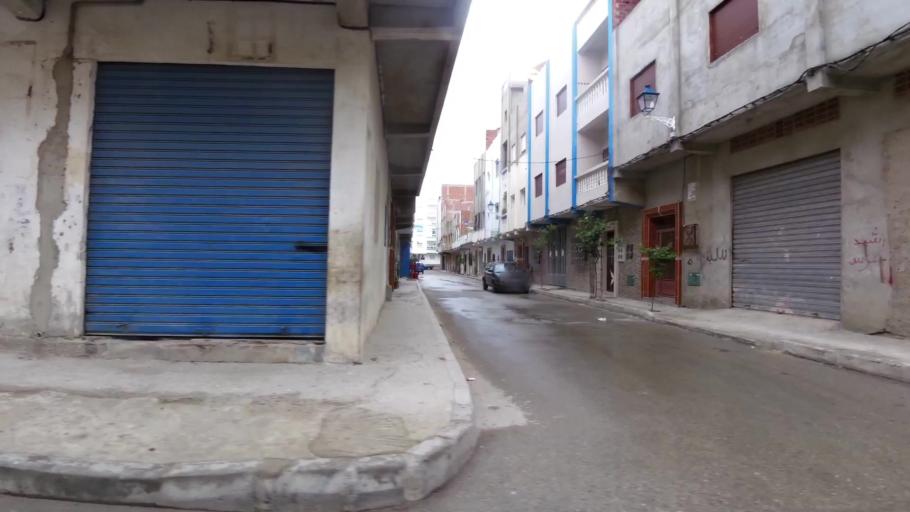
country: MA
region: Tanger-Tetouan
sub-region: Tetouan
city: Martil
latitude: 35.6273
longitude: -5.2880
